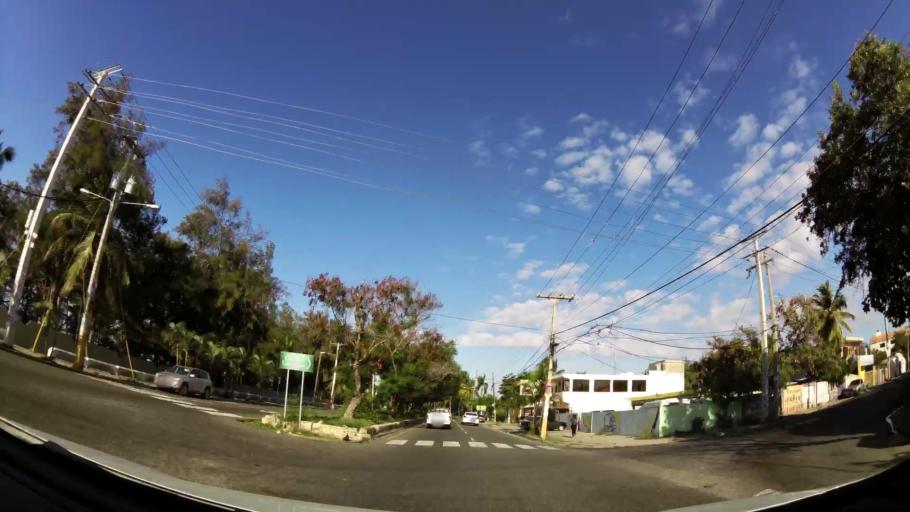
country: DO
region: Santo Domingo
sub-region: Santo Domingo
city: Santo Domingo Este
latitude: 18.4688
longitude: -69.8487
